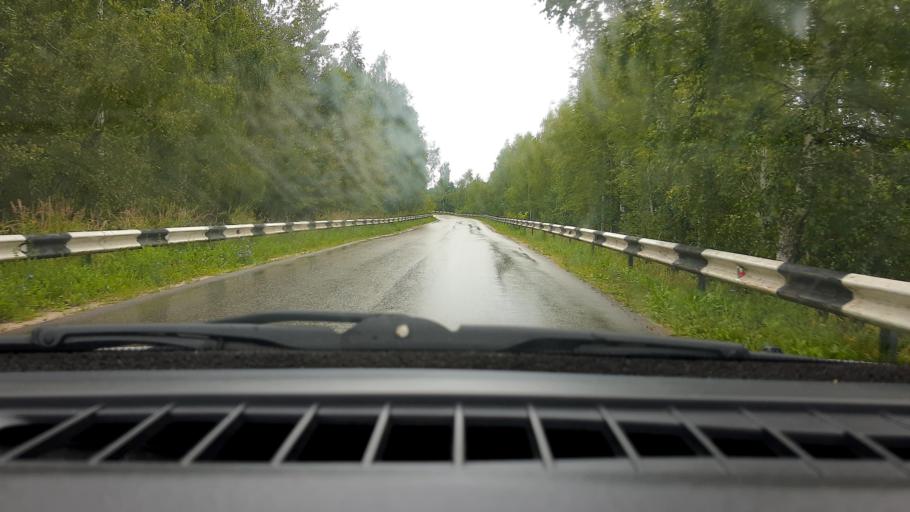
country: RU
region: Nizjnij Novgorod
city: Gorbatovka
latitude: 56.2195
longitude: 43.7566
